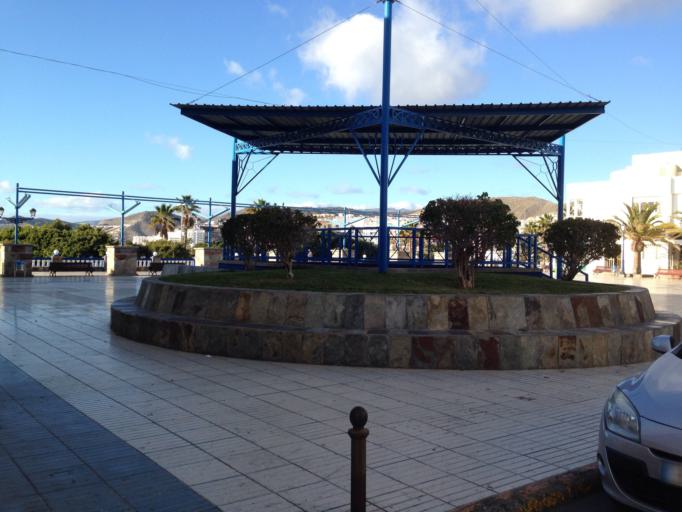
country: ES
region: Canary Islands
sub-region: Provincia de Las Palmas
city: Puerto Rico
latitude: 27.7572
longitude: -15.6823
